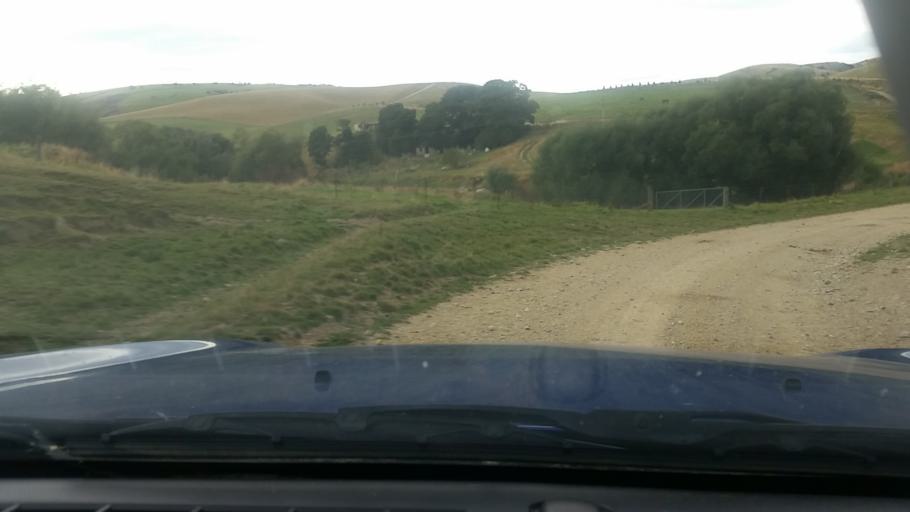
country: NZ
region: Otago
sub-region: Clutha District
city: Balclutha
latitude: -45.7374
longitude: 169.5420
